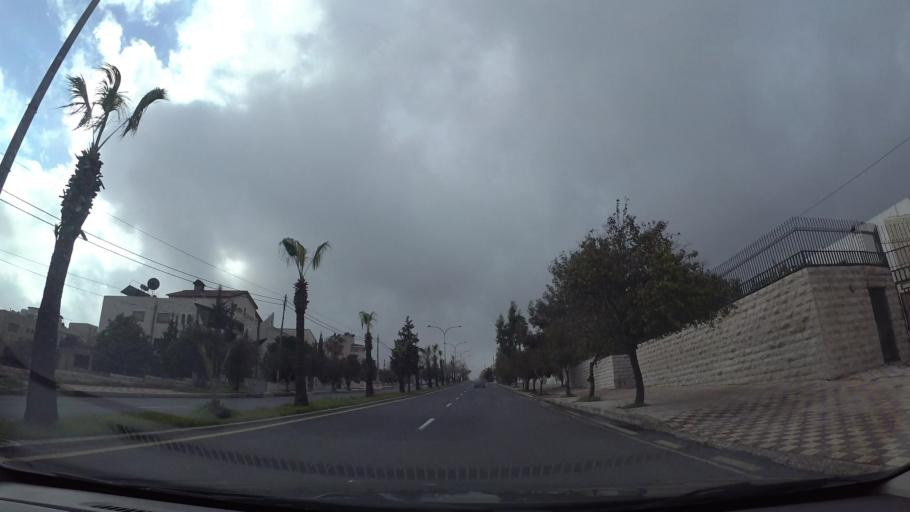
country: JO
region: Amman
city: Al Bunayyat ash Shamaliyah
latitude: 31.9511
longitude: 35.8861
